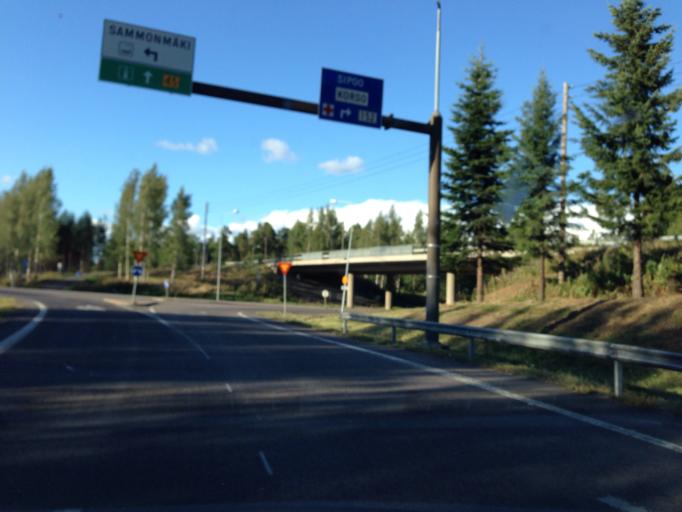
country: FI
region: Uusimaa
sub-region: Helsinki
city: Vantaa
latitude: 60.3410
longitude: 25.0027
